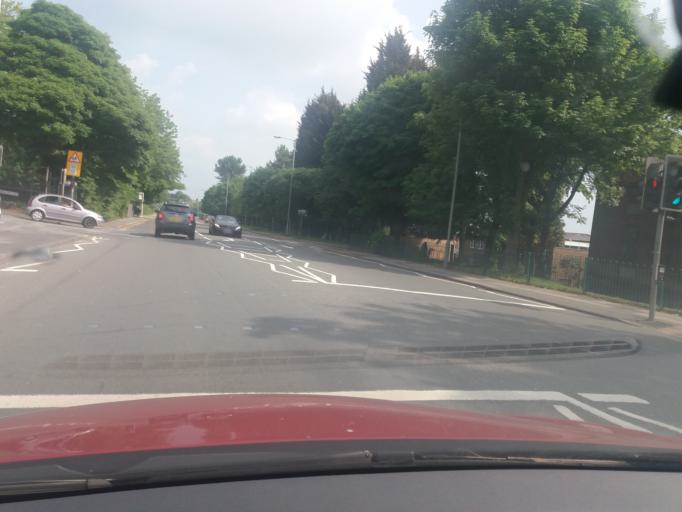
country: GB
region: England
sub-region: Borough of Bolton
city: Horwich
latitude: 53.5875
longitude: -2.5294
